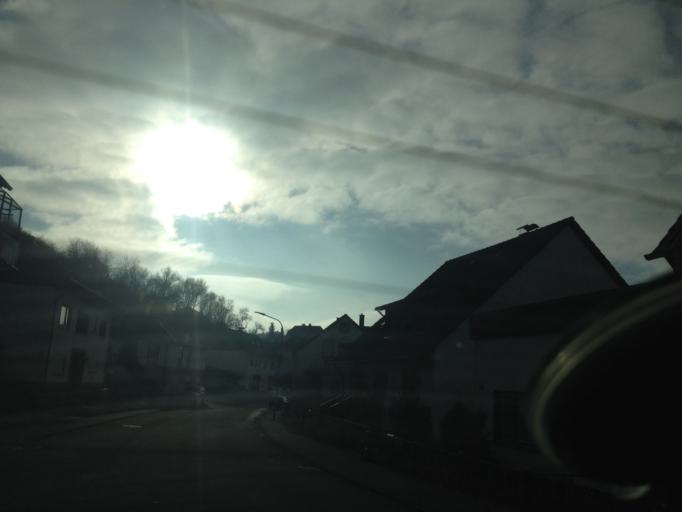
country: DE
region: Rheinland-Pfalz
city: Brucken
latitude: 49.4343
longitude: 7.3665
